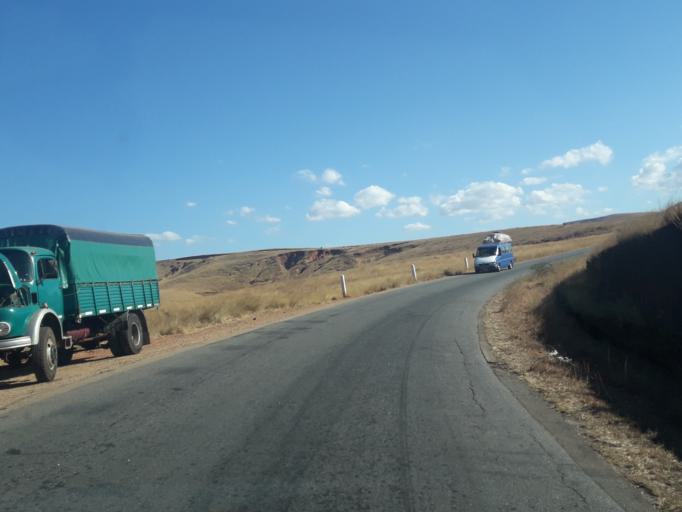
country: MG
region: Analamanga
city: Ankazobe
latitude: -17.6858
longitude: 46.9899
